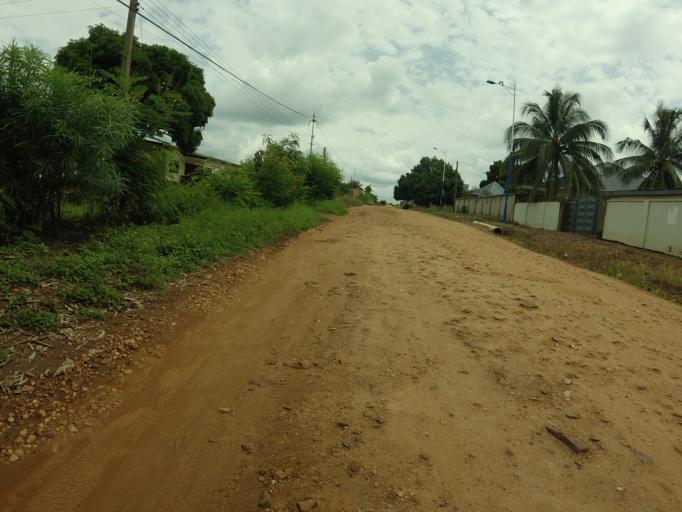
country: GH
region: Volta
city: Ho
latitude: 6.5832
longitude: 0.4615
